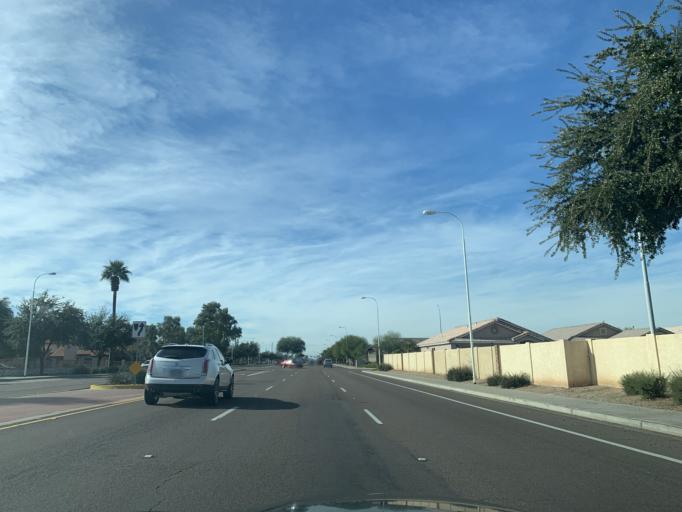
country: US
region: Arizona
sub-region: Maricopa County
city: Chandler
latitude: 33.3064
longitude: -111.8189
